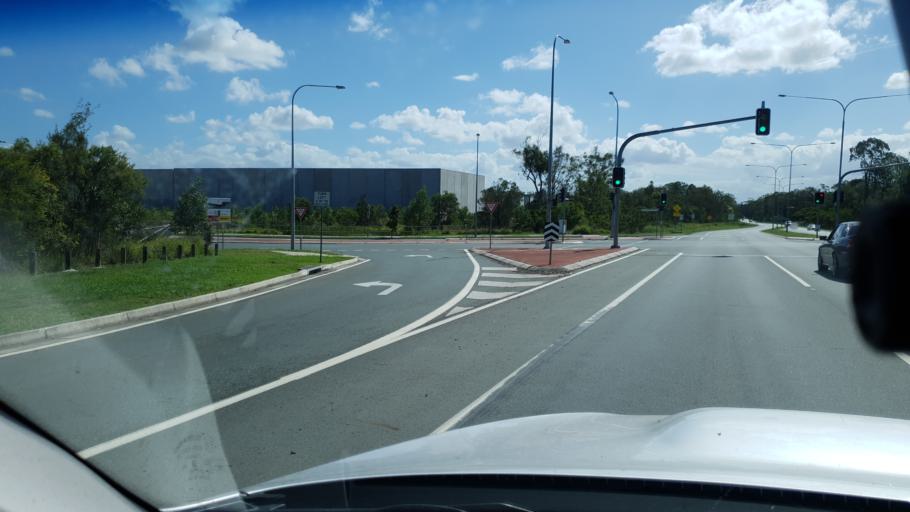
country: AU
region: Queensland
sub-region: Logan
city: Woodridge
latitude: -27.6453
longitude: 153.0949
